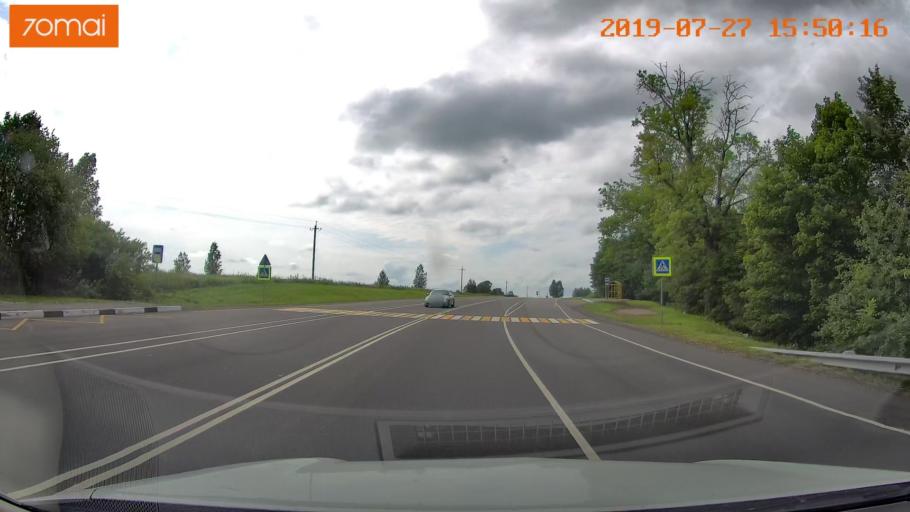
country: RU
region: Kaliningrad
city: Gusev
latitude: 54.6003
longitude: 22.0118
